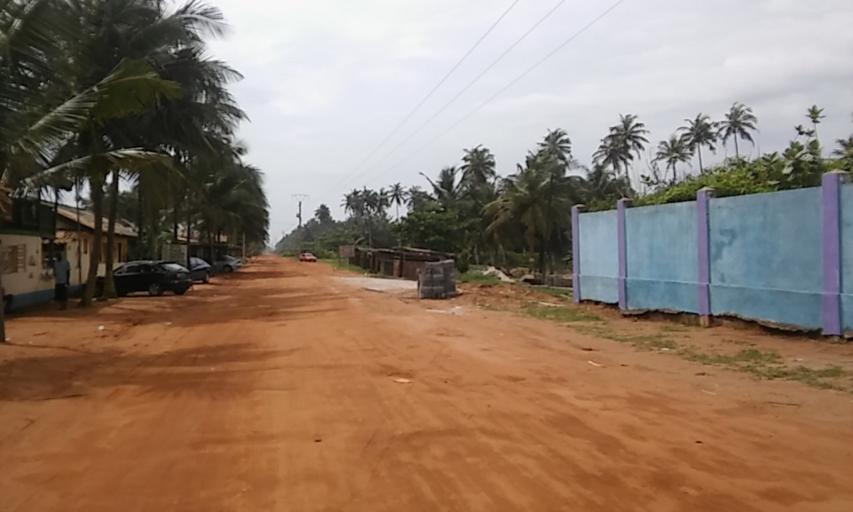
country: CI
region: Sud-Comoe
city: Grand-Bassam
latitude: 5.1977
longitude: -3.7539
